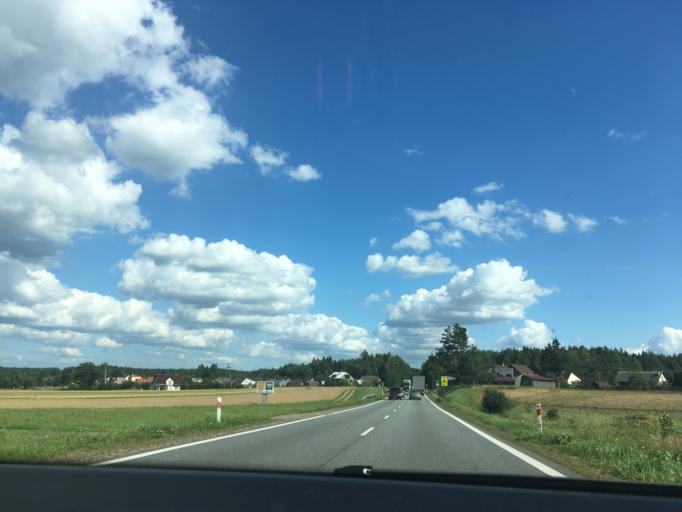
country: PL
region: Podlasie
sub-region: Powiat bialostocki
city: Wasilkow
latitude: 53.2670
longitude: 23.1262
